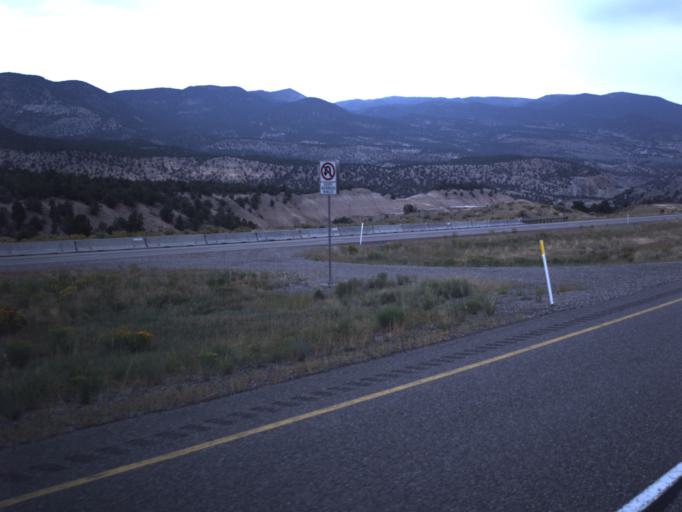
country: US
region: Utah
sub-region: Sevier County
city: Monroe
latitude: 38.5479
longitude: -112.3719
